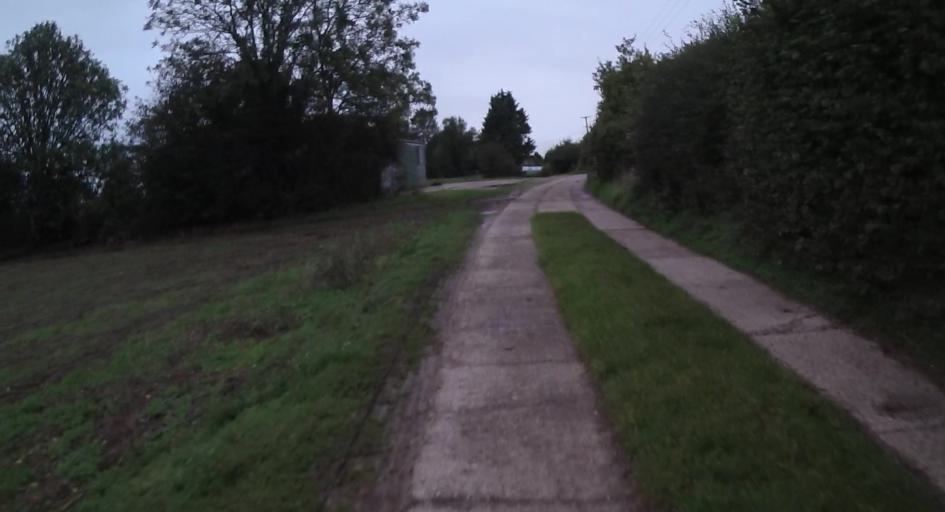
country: GB
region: England
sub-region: Hampshire
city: Basingstoke
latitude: 51.2738
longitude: -1.1357
